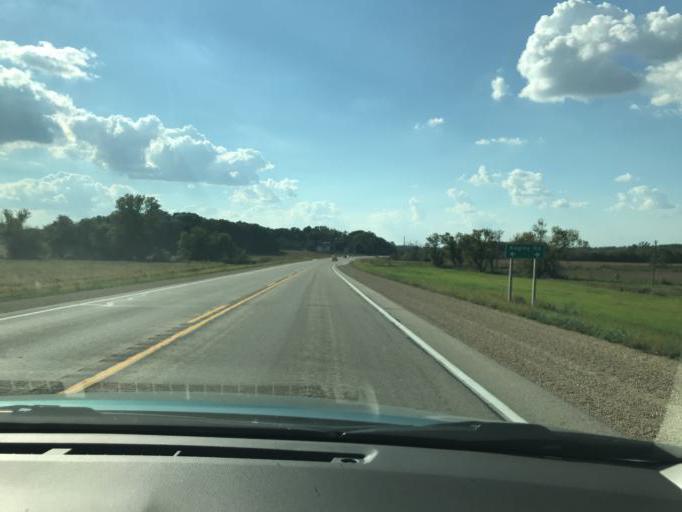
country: US
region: Wisconsin
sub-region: Green County
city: Brodhead
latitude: 42.5886
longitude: -89.4811
